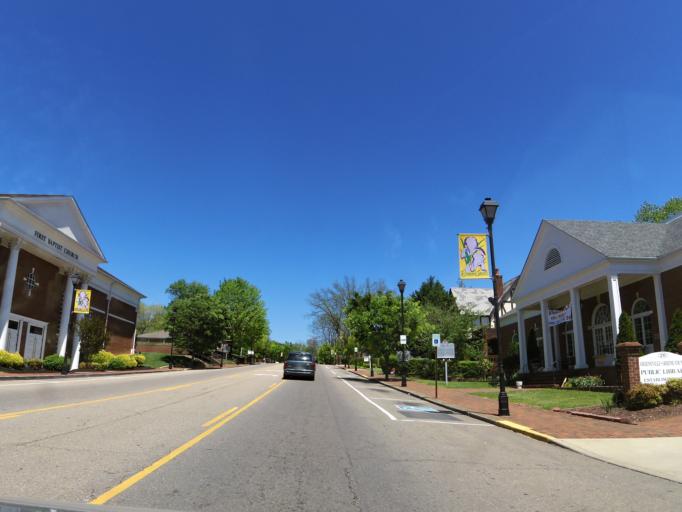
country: US
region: Tennessee
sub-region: Greene County
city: Greeneville
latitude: 36.1648
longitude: -82.8299
